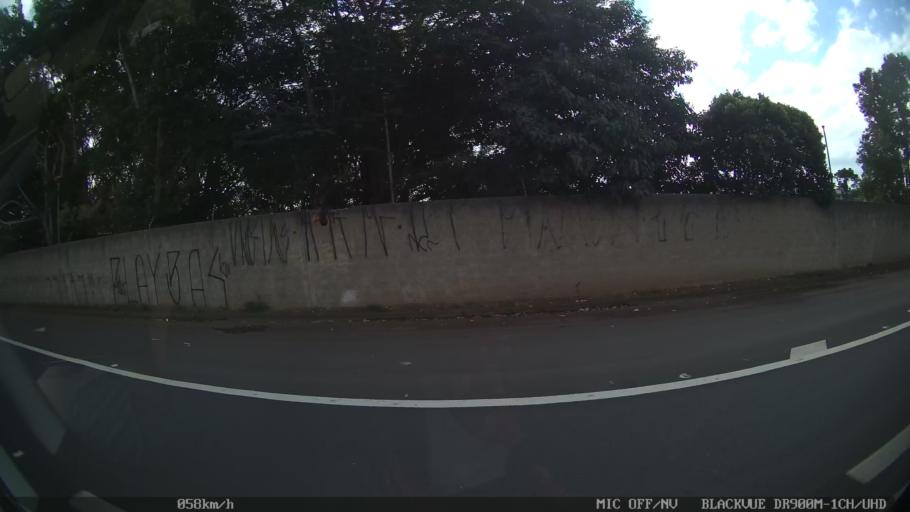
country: BR
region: Sao Paulo
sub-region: Limeira
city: Limeira
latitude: -22.5709
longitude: -47.4440
